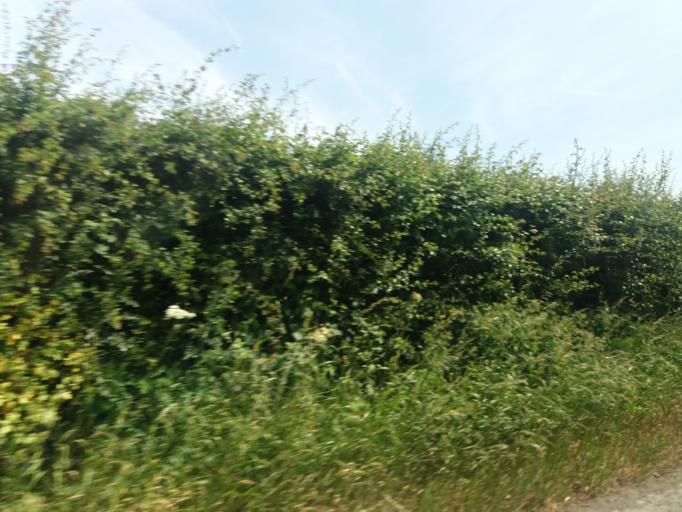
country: IE
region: Leinster
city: Lusk
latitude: 53.5426
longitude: -6.2031
